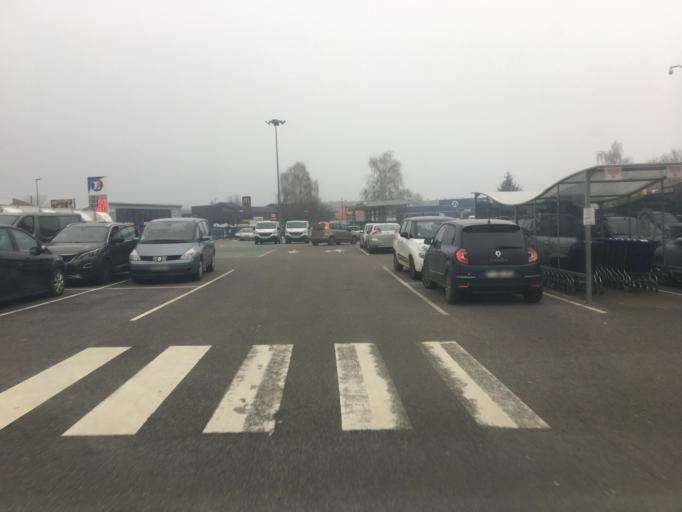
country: FR
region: Haute-Normandie
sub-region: Departement de la Seine-Maritime
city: Neufchatel-en-Bray
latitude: 49.7341
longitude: 1.4331
